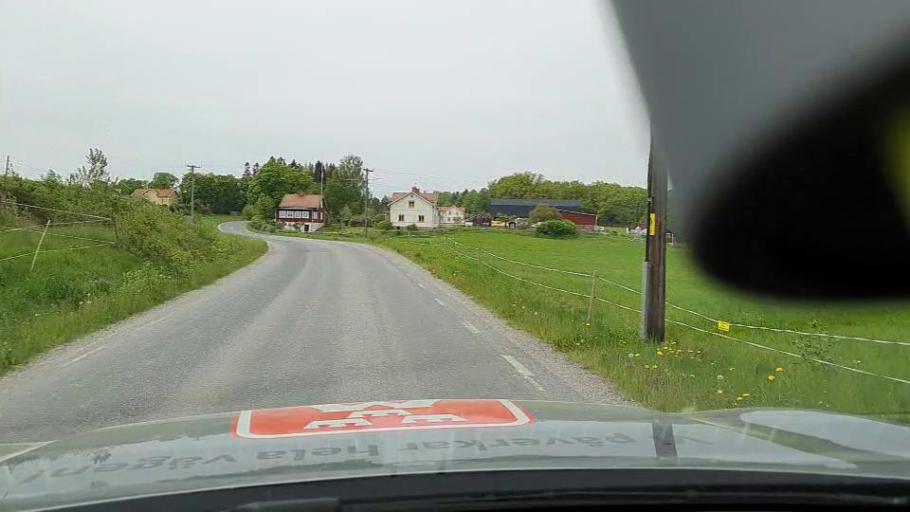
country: SE
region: Soedermanland
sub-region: Flens Kommun
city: Flen
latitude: 59.1025
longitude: 16.5508
